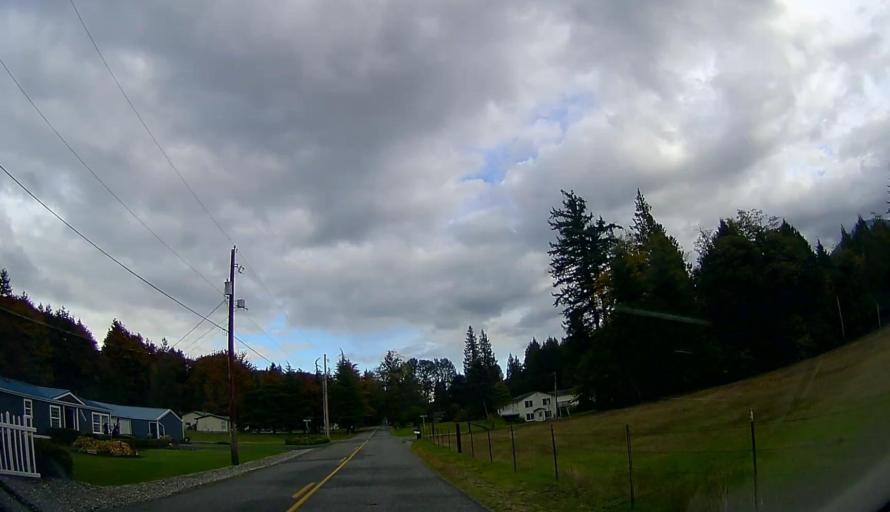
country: US
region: Washington
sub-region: Skagit County
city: Sedro-Woolley
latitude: 48.5339
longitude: -122.0285
